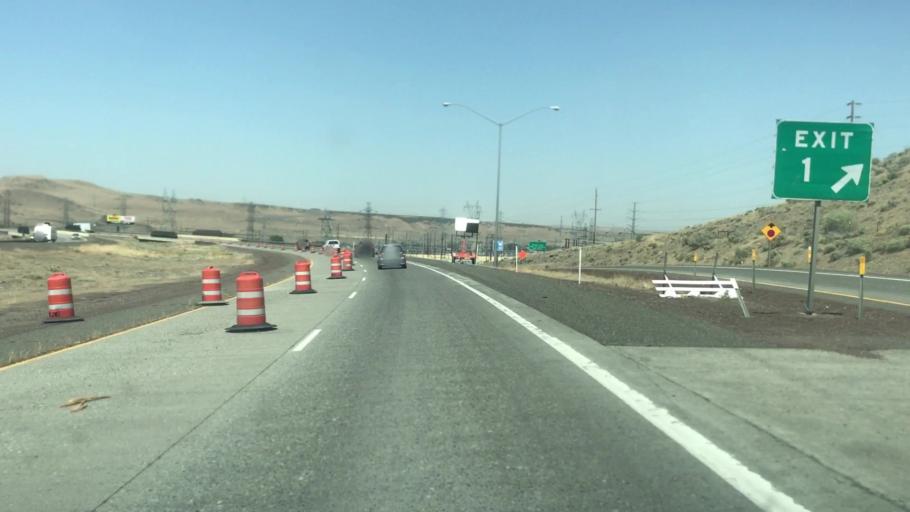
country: US
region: Oregon
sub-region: Umatilla County
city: Umatilla
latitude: 45.9156
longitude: -119.3217
